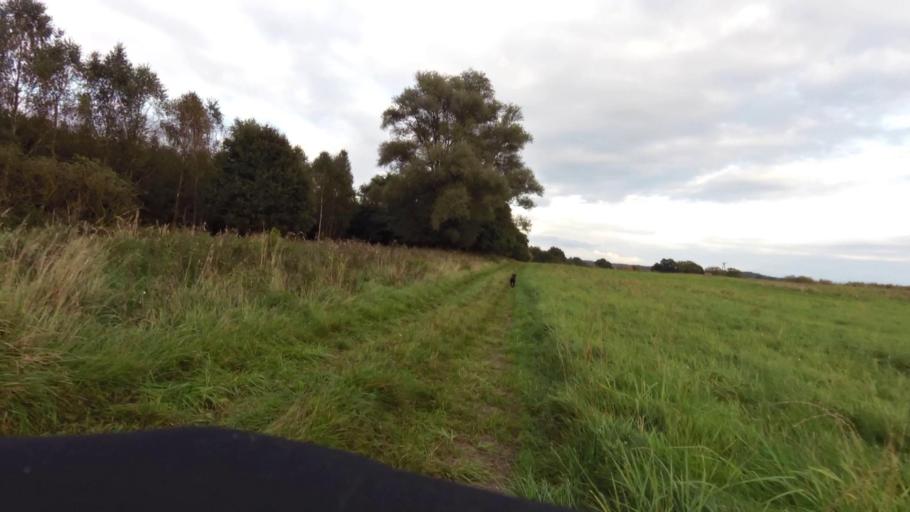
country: PL
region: West Pomeranian Voivodeship
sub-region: Powiat stargardzki
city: Dobrzany
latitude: 53.3824
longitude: 15.4018
